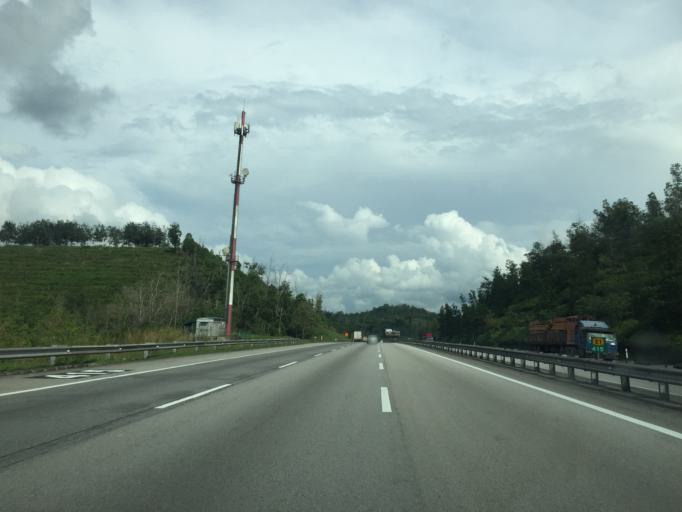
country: MY
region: Selangor
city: Batang Berjuntai
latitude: 3.5337
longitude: 101.5206
